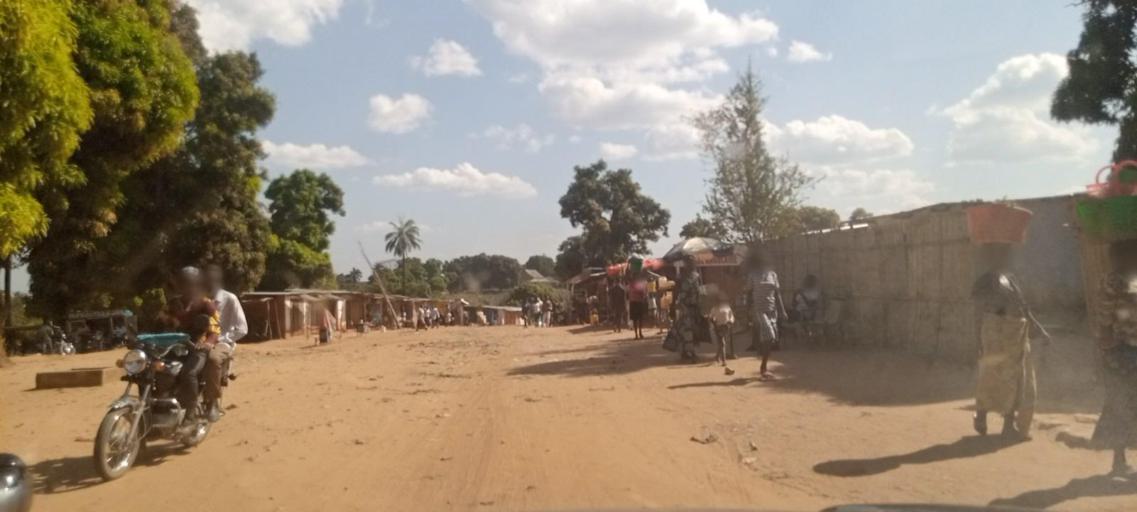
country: CD
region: Kasai-Oriental
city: Kabinda
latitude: -6.1280
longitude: 24.4980
